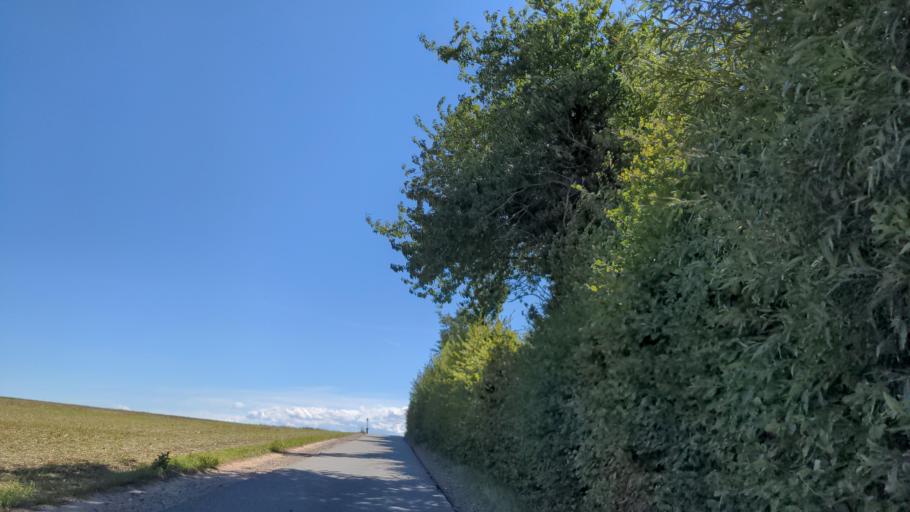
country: DE
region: Schleswig-Holstein
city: Altenkrempe
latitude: 54.1691
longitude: 10.7998
